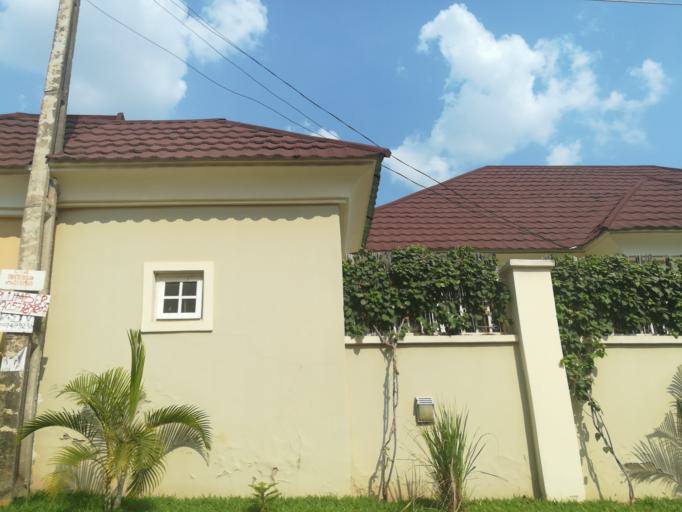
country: NG
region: Abuja Federal Capital Territory
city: Abuja
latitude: 9.0802
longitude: 7.4149
